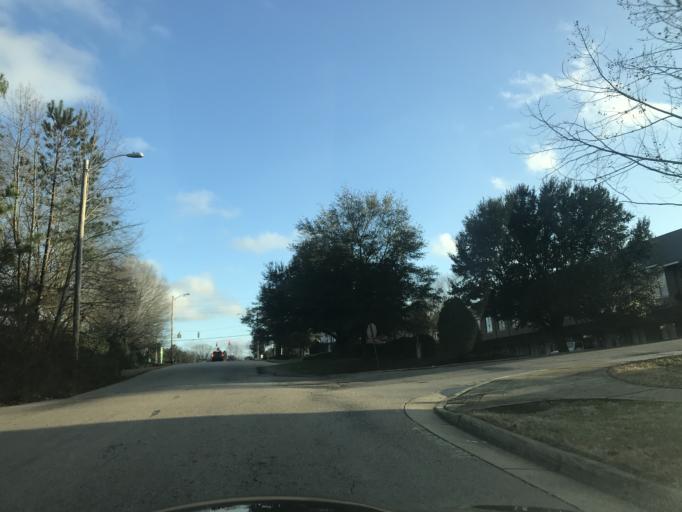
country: US
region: North Carolina
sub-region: Wake County
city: Wake Forest
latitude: 35.9508
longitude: -78.5319
